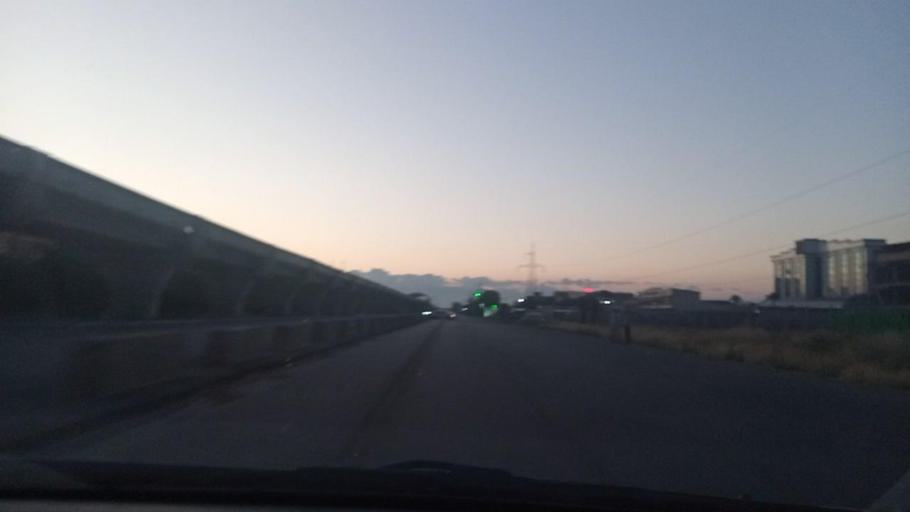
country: UZ
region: Toshkent Shahri
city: Bektemir
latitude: 41.2440
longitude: 69.2920
